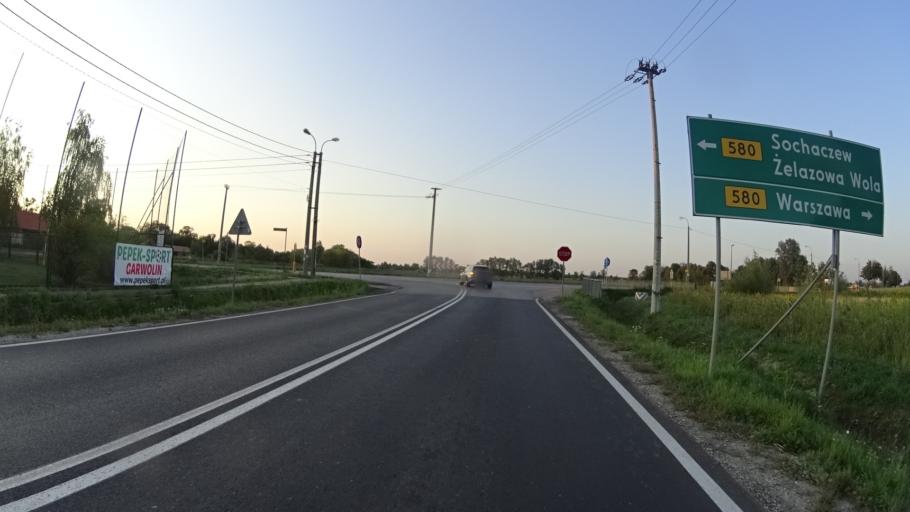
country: PL
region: Masovian Voivodeship
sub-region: Powiat warszawski zachodni
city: Truskaw
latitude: 52.2526
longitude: 20.7412
